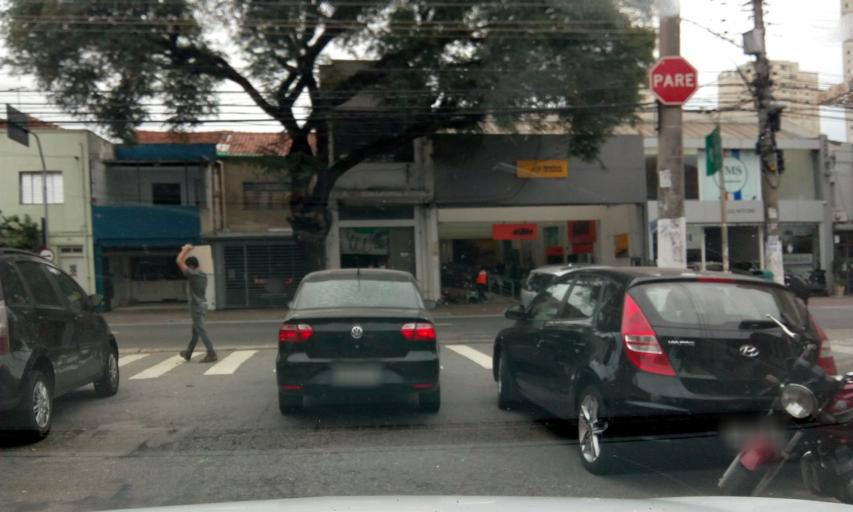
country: BR
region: Sao Paulo
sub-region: Sao Paulo
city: Sao Paulo
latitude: -23.5253
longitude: -46.6868
